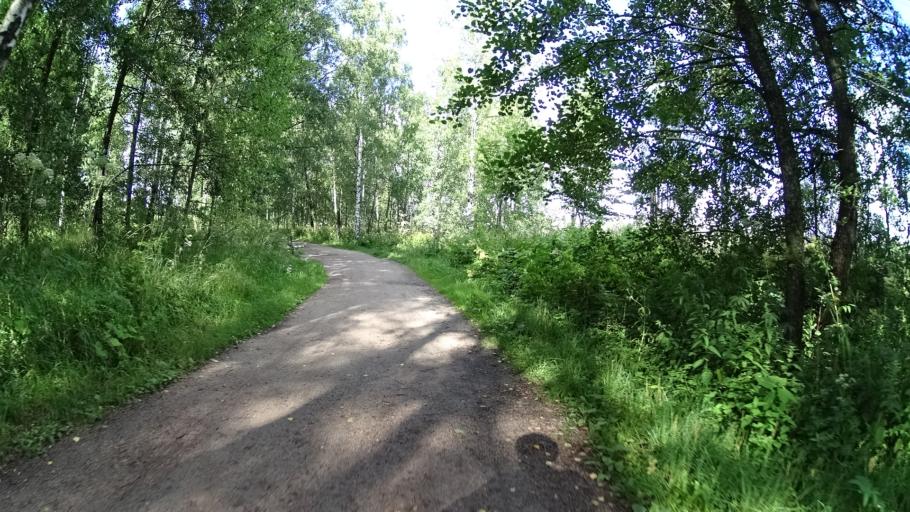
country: FI
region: Uusimaa
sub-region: Helsinki
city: Teekkarikylae
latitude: 60.1984
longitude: 24.8880
